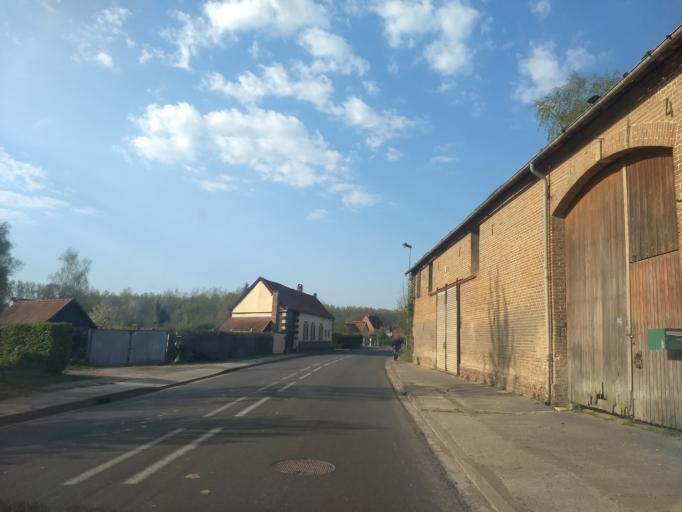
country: FR
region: Picardie
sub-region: Departement de la Somme
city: Corbie
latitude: 50.0030
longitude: 2.4728
